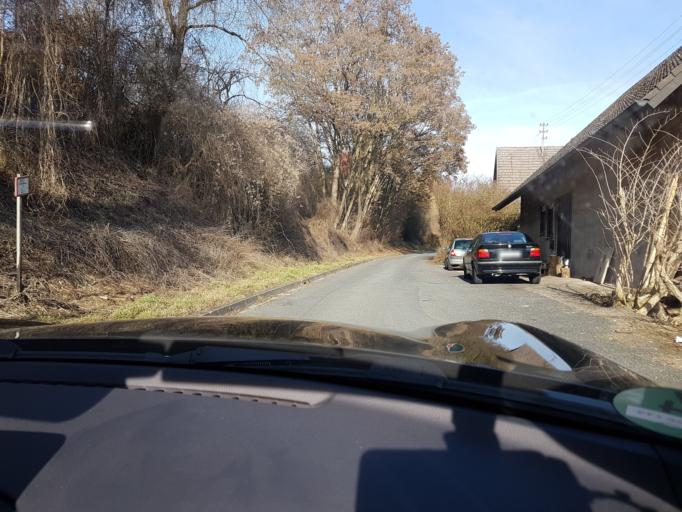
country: DE
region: Baden-Wuerttemberg
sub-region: Karlsruhe Region
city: Osterburken
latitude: 49.4343
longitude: 9.4253
